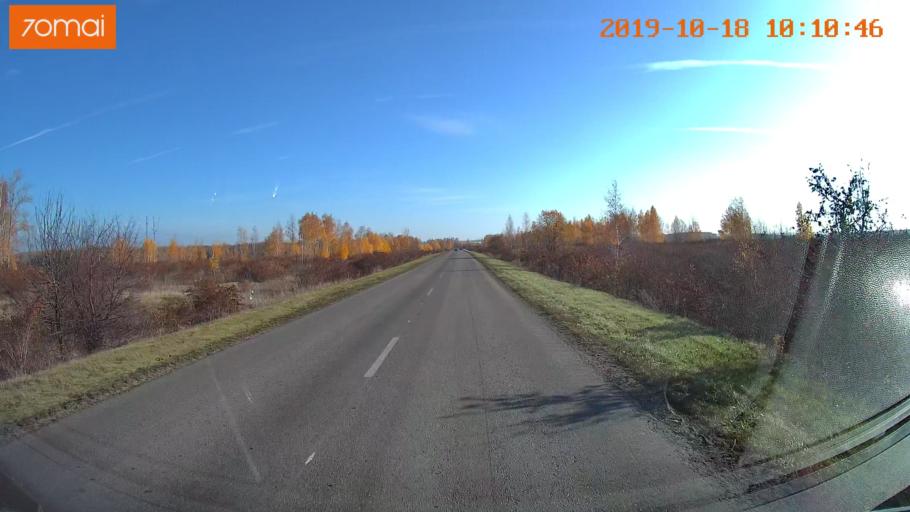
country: RU
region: Tula
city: Kurkino
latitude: 53.3799
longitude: 38.4835
